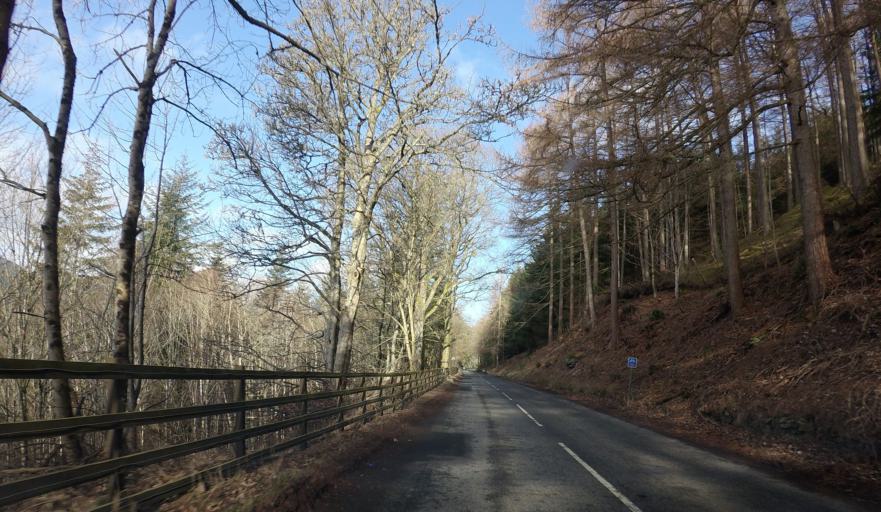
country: GB
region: Scotland
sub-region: Perth and Kinross
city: Bankfoot
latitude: 56.5781
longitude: -3.6185
